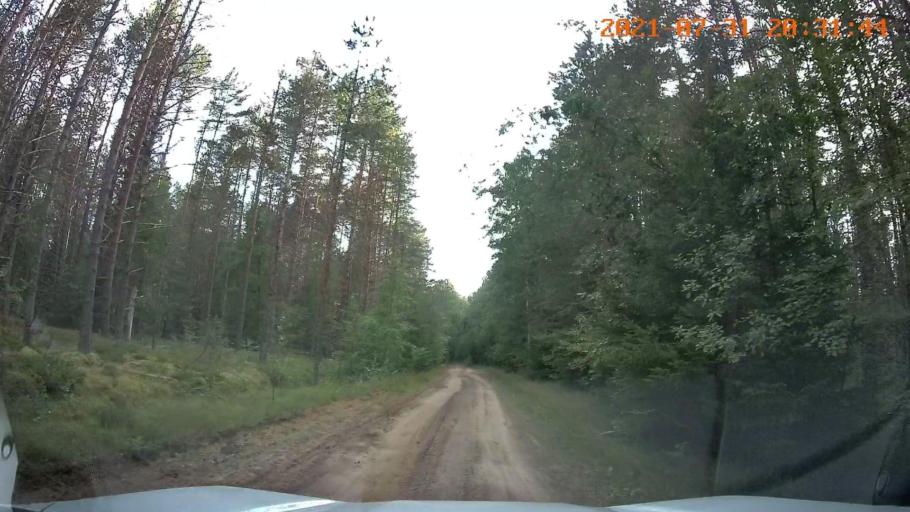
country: RU
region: Republic of Karelia
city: Pudozh
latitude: 61.6613
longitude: 36.2780
